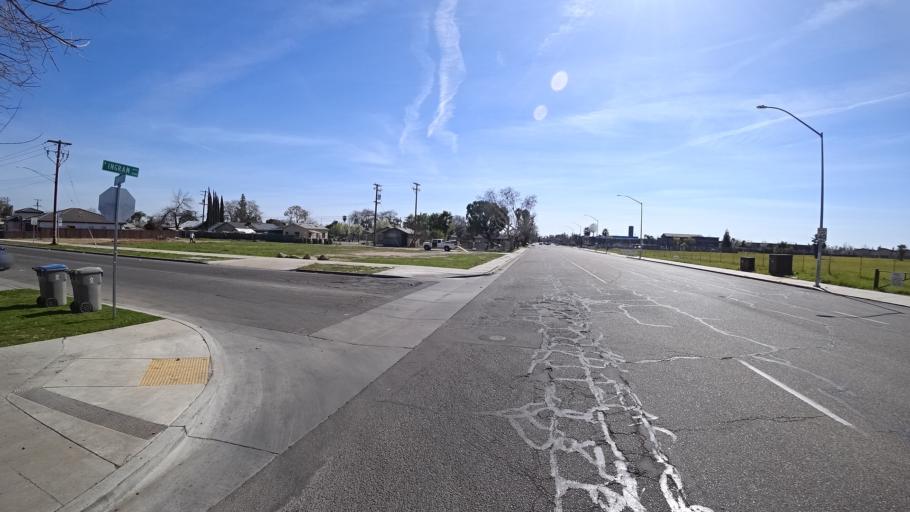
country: US
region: California
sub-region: Fresno County
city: Fresno
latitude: 36.8427
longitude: -119.8018
